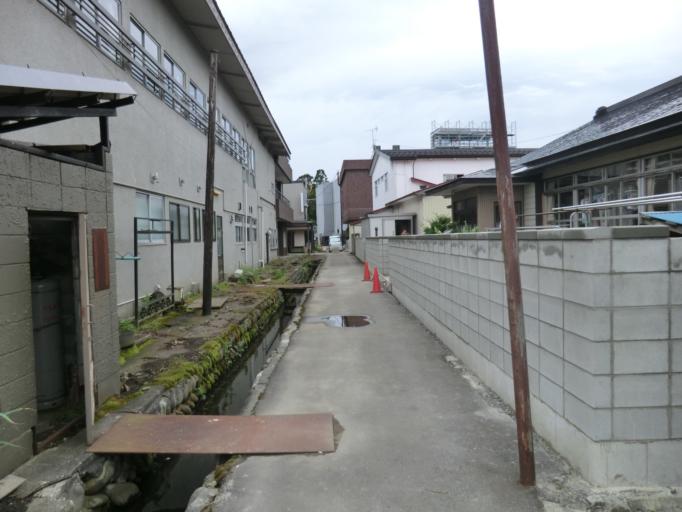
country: JP
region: Fukushima
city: Inawashiro
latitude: 37.5358
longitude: 140.0745
